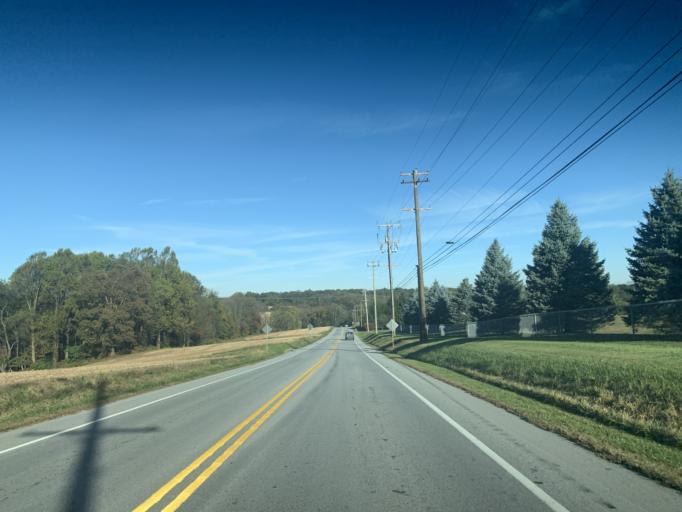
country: US
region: Pennsylvania
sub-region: Chester County
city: Parkesburg
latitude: 39.9404
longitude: -75.9121
